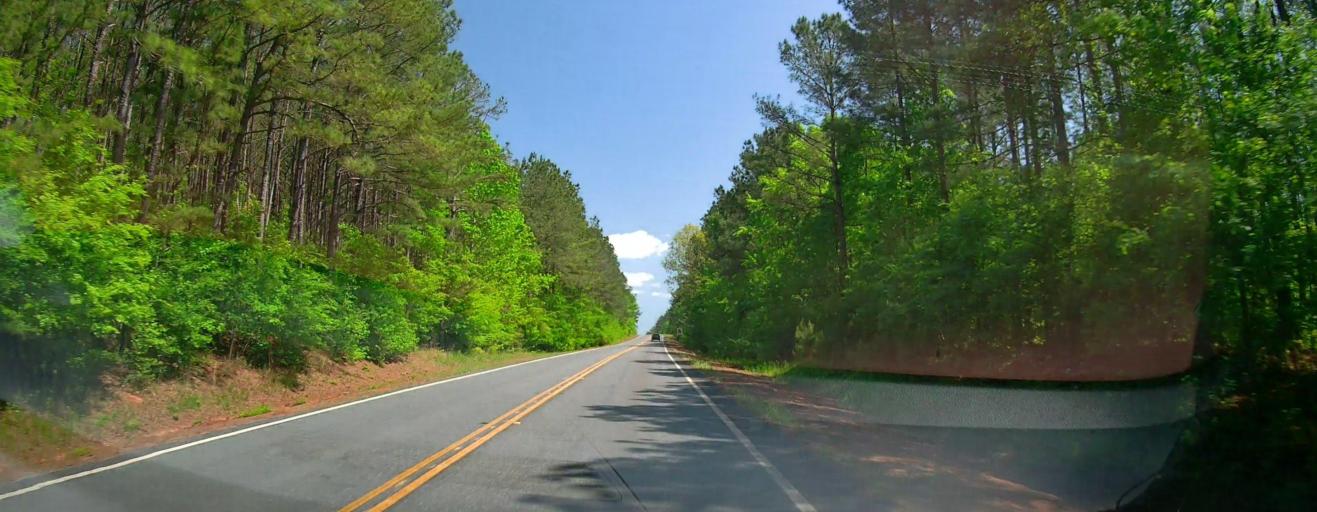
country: US
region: Georgia
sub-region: Putnam County
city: Eatonton
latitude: 33.2171
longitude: -83.4875
